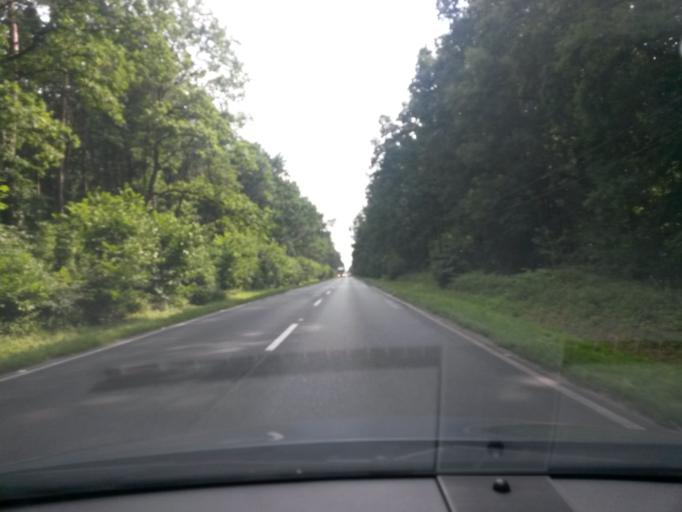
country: PL
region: Greater Poland Voivodeship
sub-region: Powiat poznanski
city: Kornik
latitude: 52.2126
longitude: 17.0706
